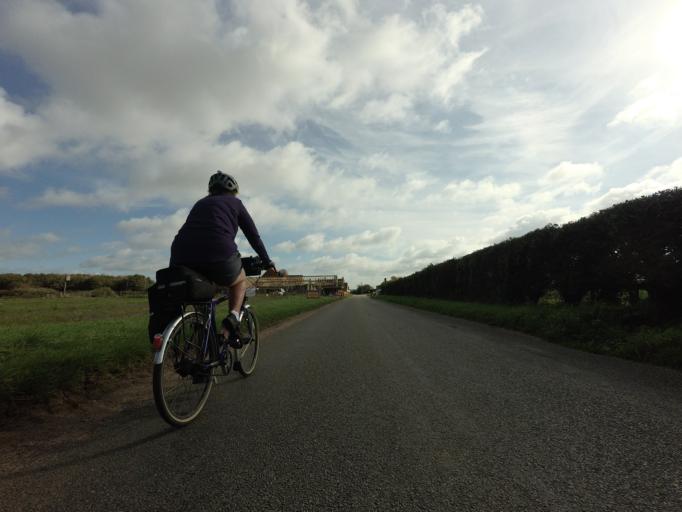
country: GB
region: England
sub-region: Norfolk
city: Wells-next-the-Sea
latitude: 52.9112
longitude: 0.7183
